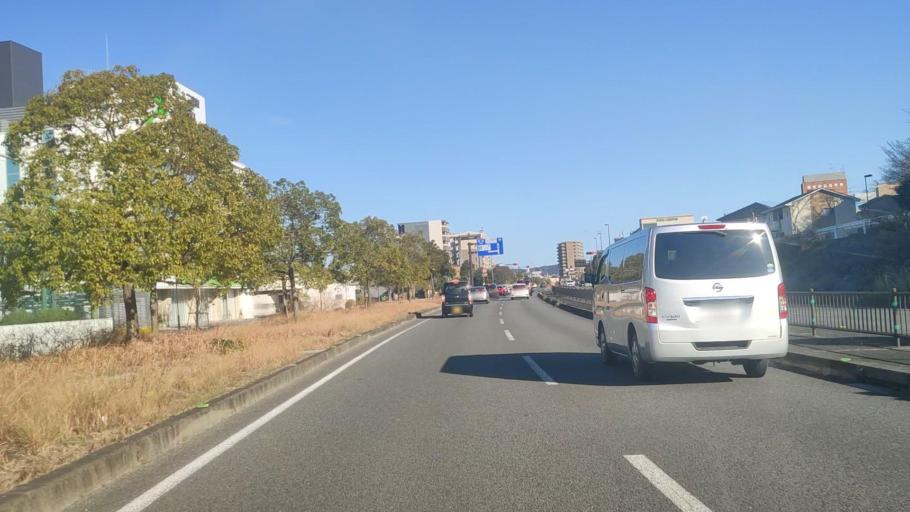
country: JP
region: Oita
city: Oita
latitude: 33.2276
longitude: 131.6019
